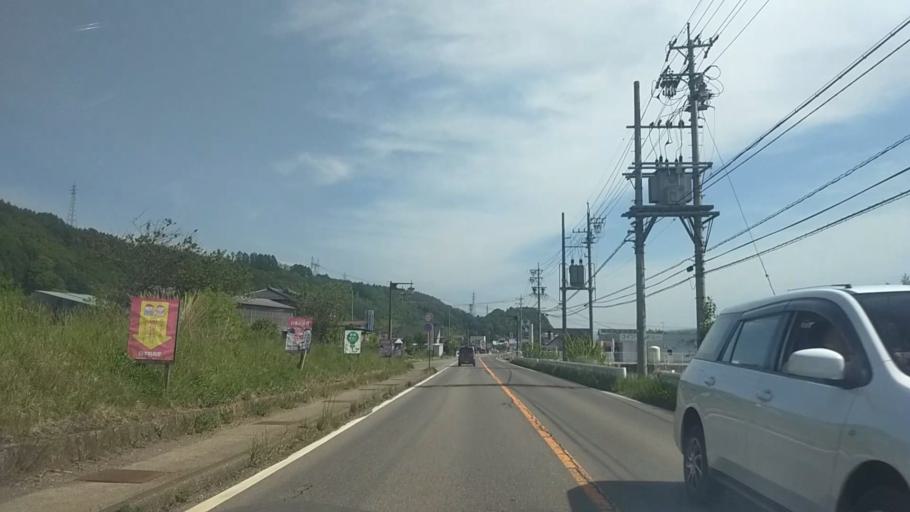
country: JP
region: Nagano
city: Saku
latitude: 36.1467
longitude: 138.4739
